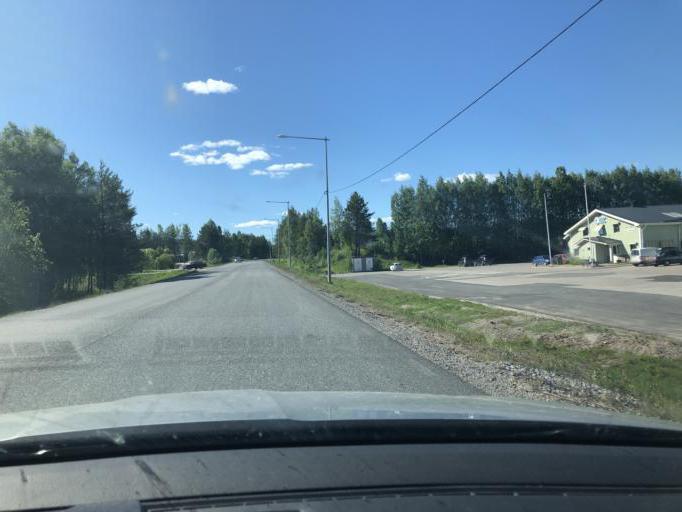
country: SE
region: Norrbotten
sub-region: Kalix Kommun
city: Kalix
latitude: 65.8586
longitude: 23.1663
